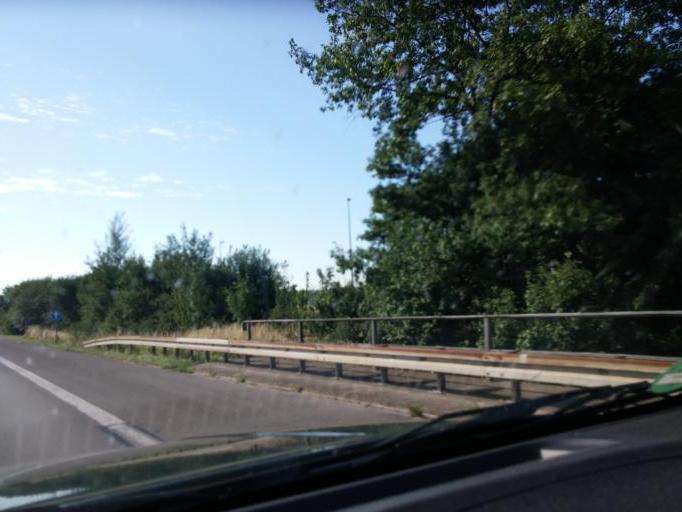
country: DE
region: North Rhine-Westphalia
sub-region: Regierungsbezirk Dusseldorf
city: Monchengladbach
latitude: 51.1877
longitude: 6.3875
